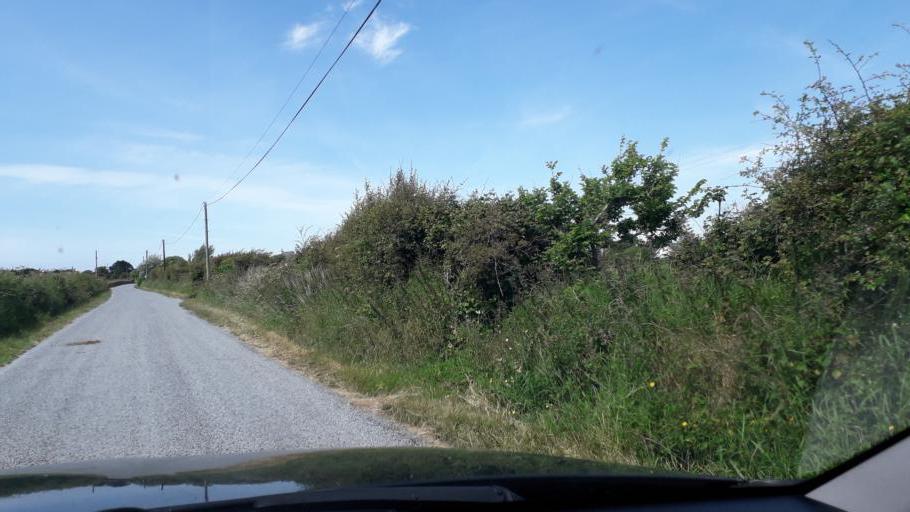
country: IE
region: Leinster
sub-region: Loch Garman
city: Loch Garman
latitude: 52.1919
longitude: -6.5500
